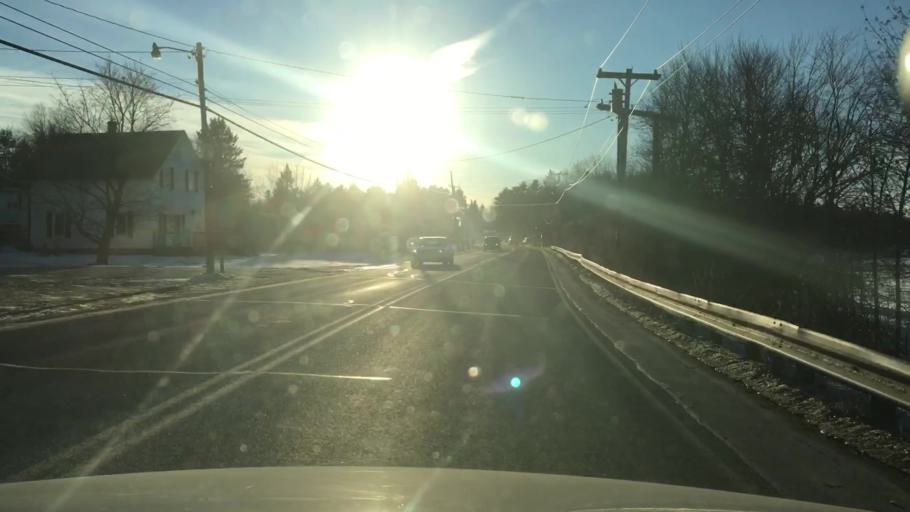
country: US
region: Maine
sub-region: Penobscot County
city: Eddington
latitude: 44.8219
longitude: -68.6956
